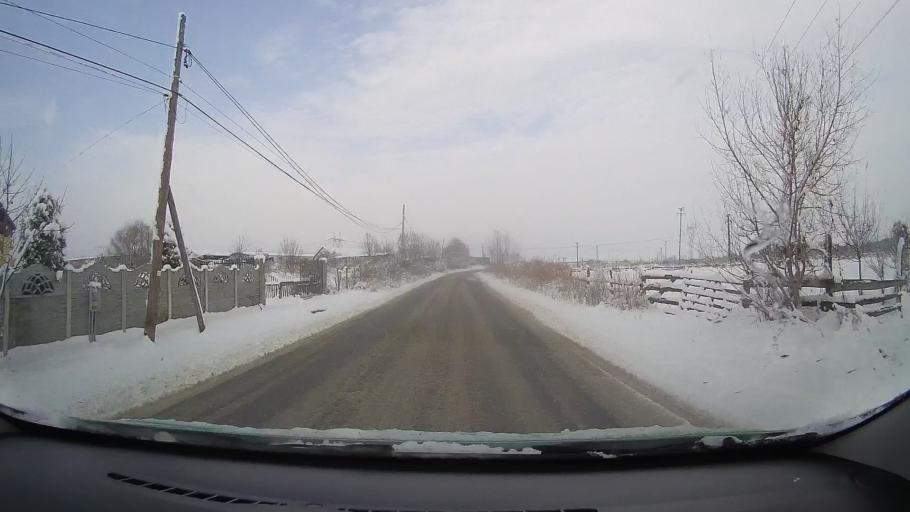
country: RO
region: Alba
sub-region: Comuna Pianu
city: Pianu de Jos
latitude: 45.9449
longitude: 23.4804
